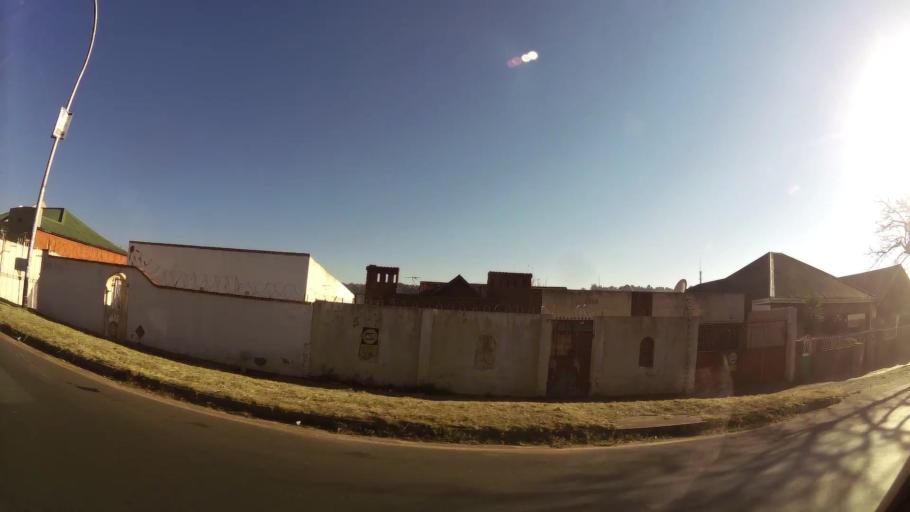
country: ZA
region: Gauteng
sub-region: City of Johannesburg Metropolitan Municipality
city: Johannesburg
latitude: -26.1954
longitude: 28.0735
